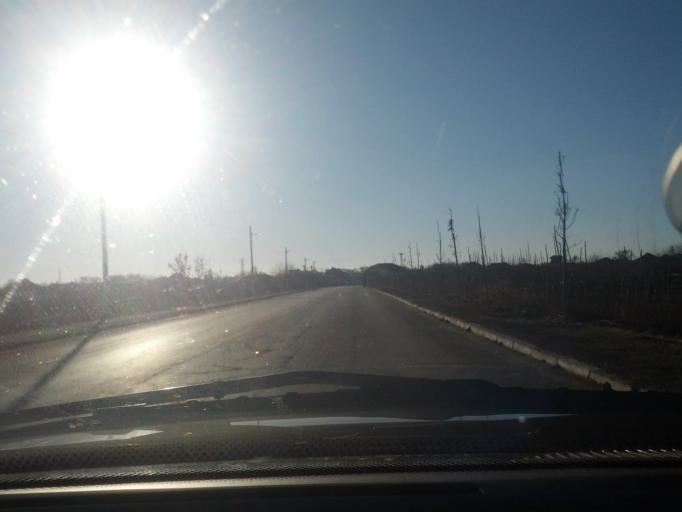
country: BG
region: Vratsa
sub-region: Obshtina Miziya
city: Miziya
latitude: 43.7019
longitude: 23.8217
